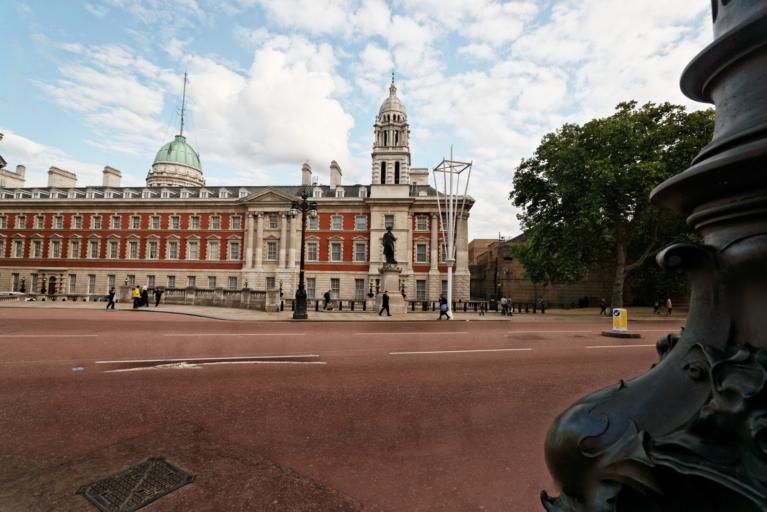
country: GB
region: England
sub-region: Greater London
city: London
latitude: 51.5066
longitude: -0.1294
